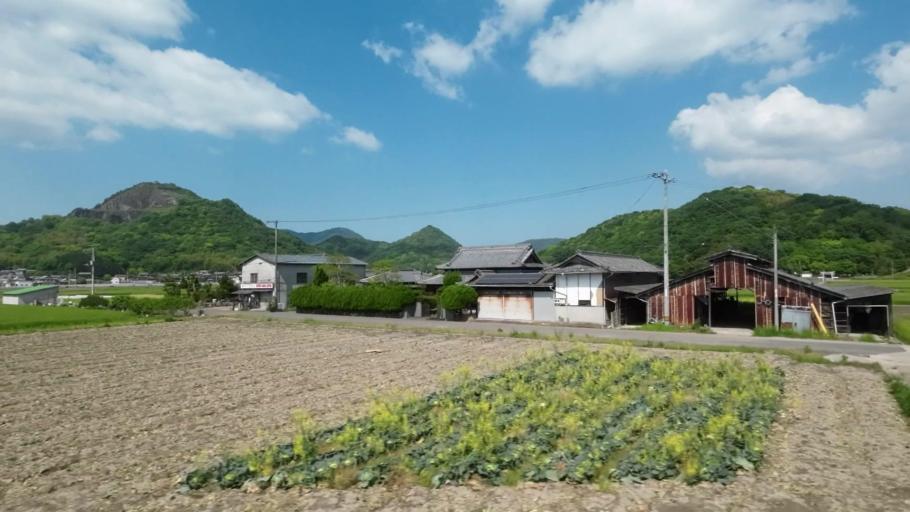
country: JP
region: Kagawa
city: Tadotsu
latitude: 34.1921
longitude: 133.7131
